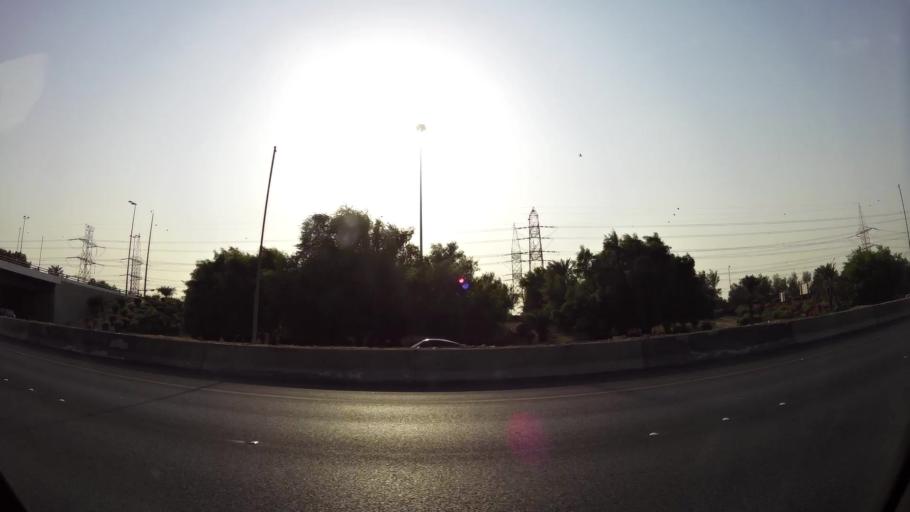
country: KW
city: Bayan
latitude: 29.2808
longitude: 48.0346
